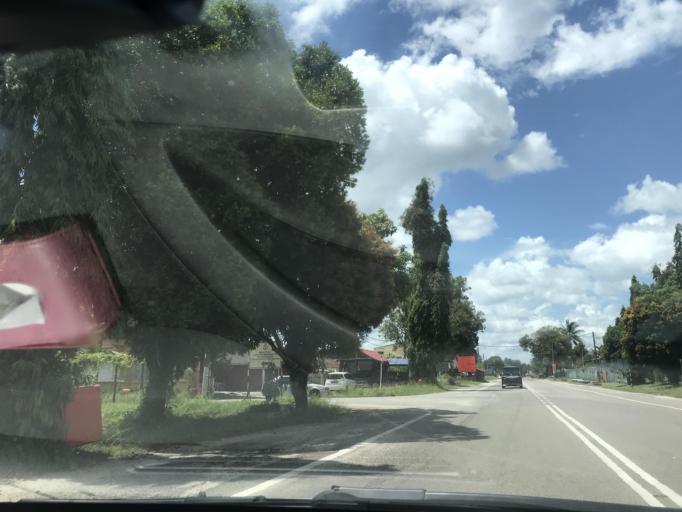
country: TH
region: Narathiwat
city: Tak Bai
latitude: 6.2294
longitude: 102.0939
